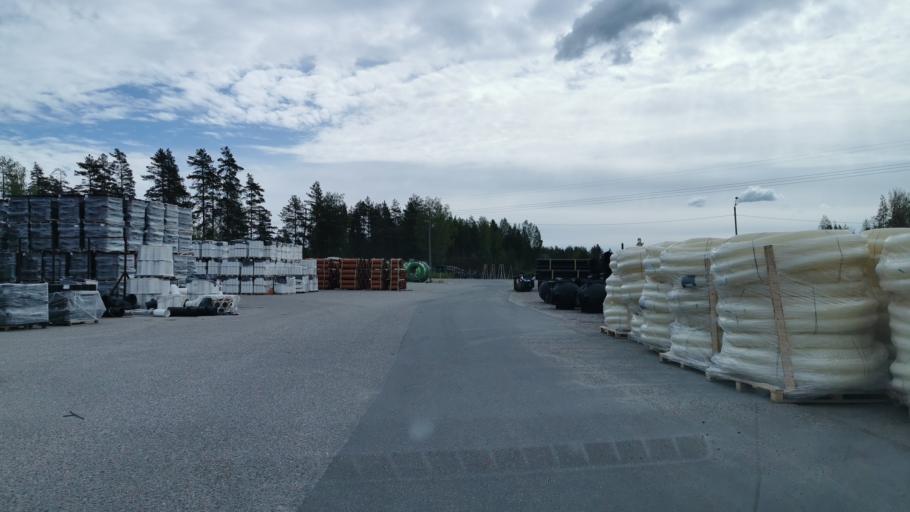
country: FI
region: Paijanne Tavastia
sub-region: Lahti
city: Nastola
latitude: 60.9311
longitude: 25.9685
